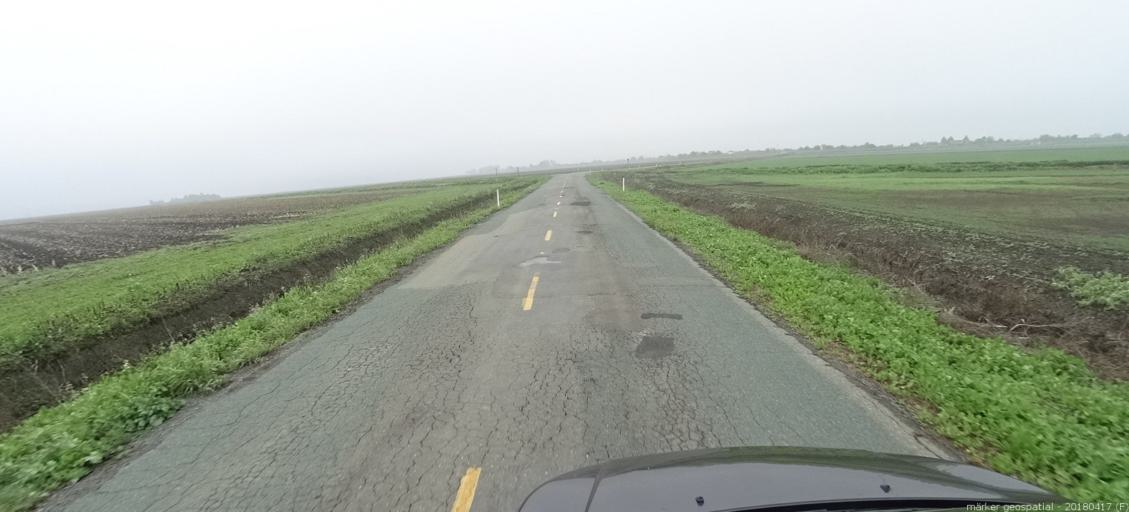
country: US
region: California
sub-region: Sacramento County
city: Walnut Grove
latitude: 38.2034
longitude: -121.5315
